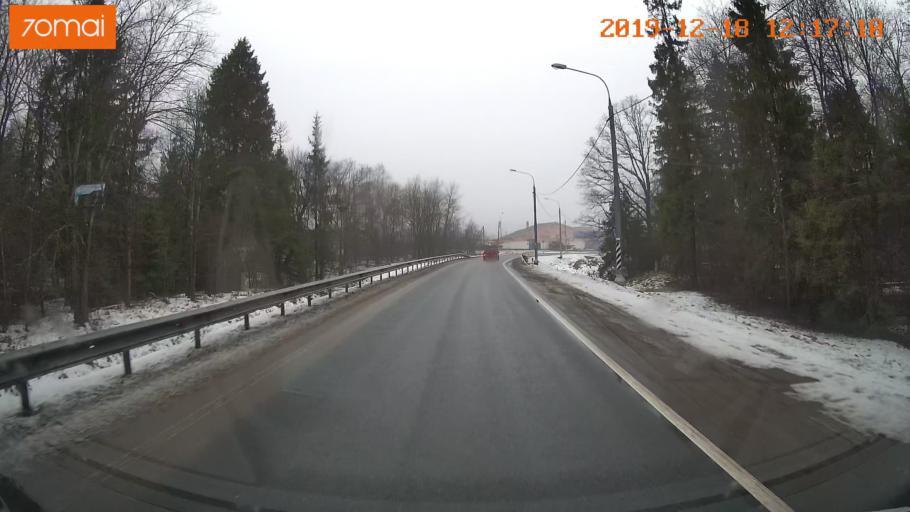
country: RU
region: Moskovskaya
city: Novopetrovskoye
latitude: 55.9811
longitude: 36.4552
